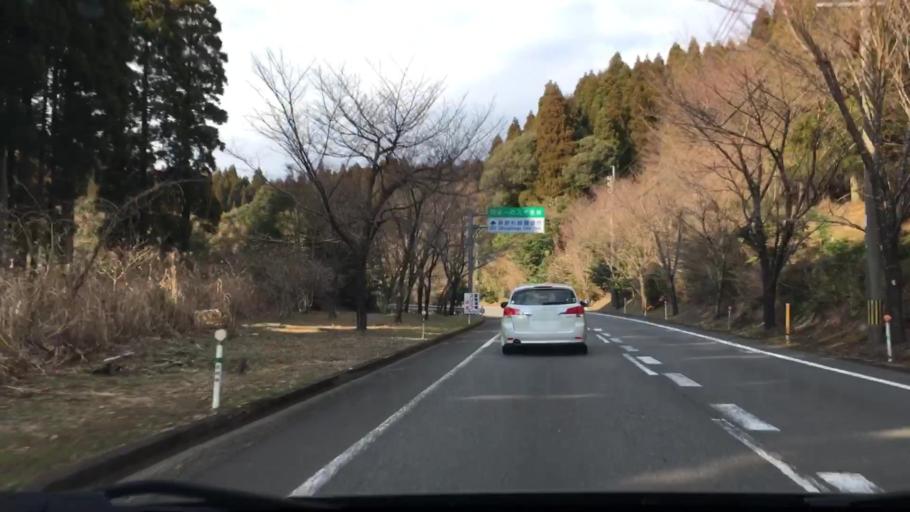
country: JP
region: Miyazaki
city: Miyazaki-shi
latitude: 31.7782
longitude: 131.3302
